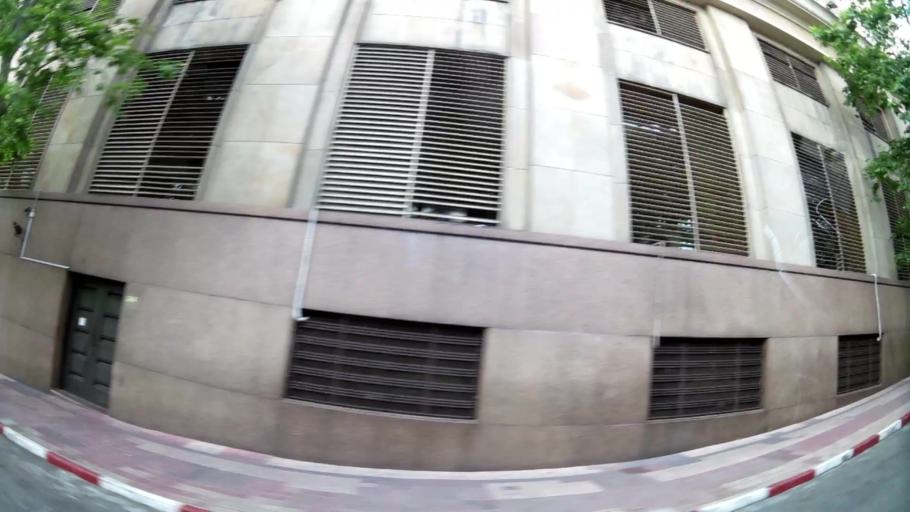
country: UY
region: Montevideo
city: Montevideo
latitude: -34.9017
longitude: -56.1930
